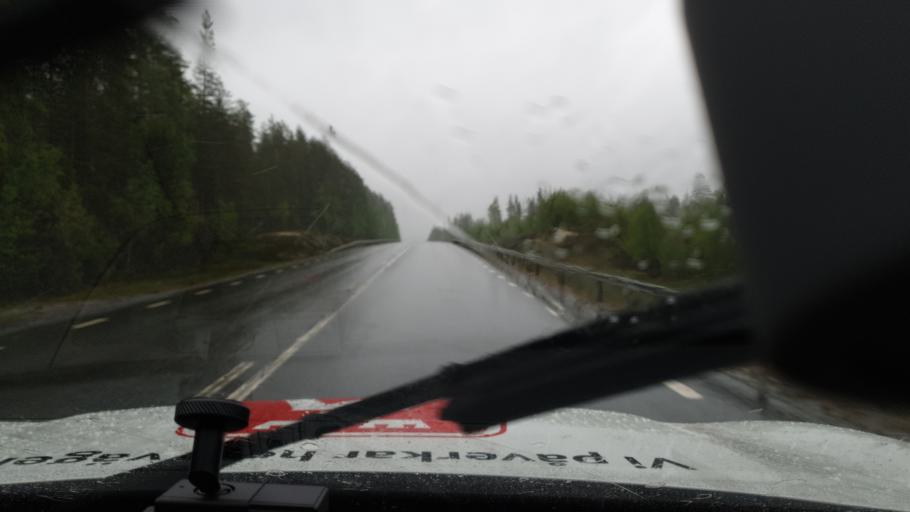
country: SE
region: Vaesterbotten
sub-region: Vannas Kommun
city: Vannasby
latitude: 64.0539
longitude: 19.9967
